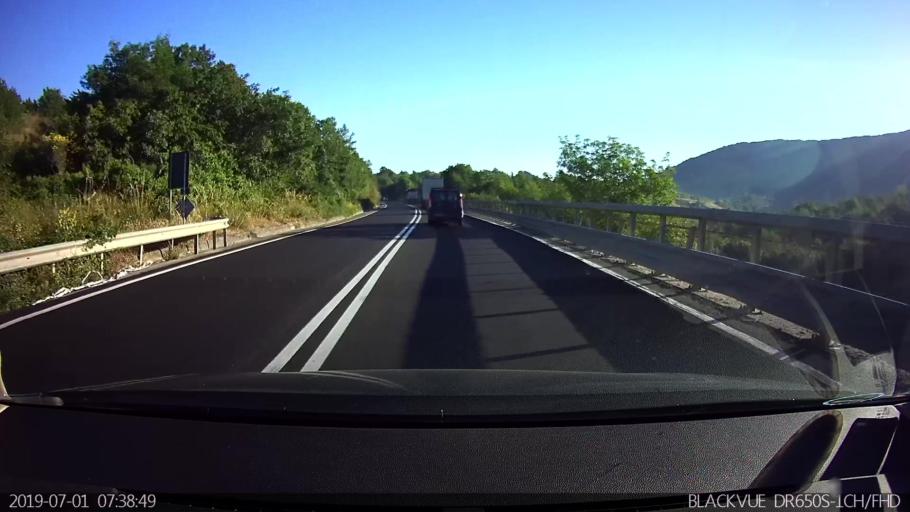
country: IT
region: Latium
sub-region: Provincia di Frosinone
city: Giuliano di Roma
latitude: 41.5456
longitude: 13.2695
